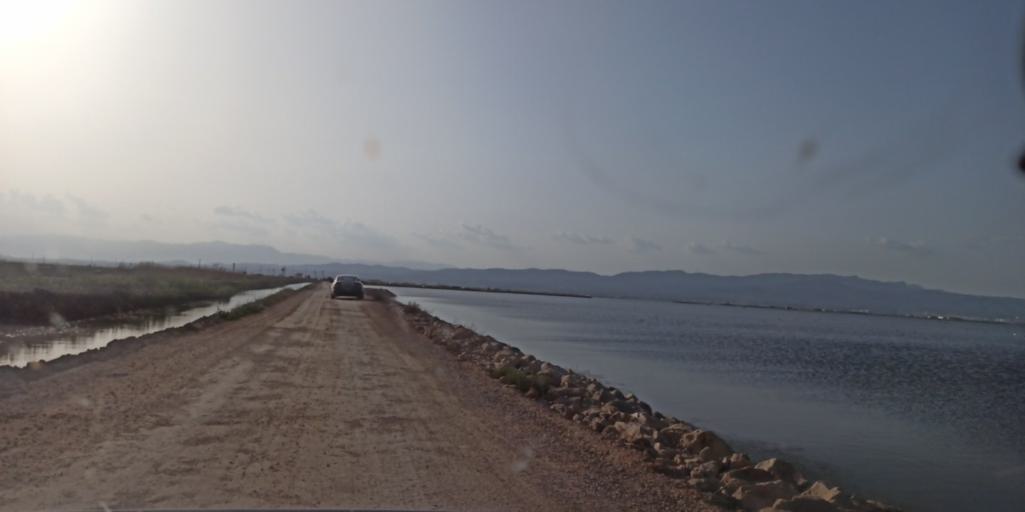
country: ES
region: Catalonia
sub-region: Provincia de Tarragona
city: Deltebre
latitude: 40.7649
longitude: 0.7464
